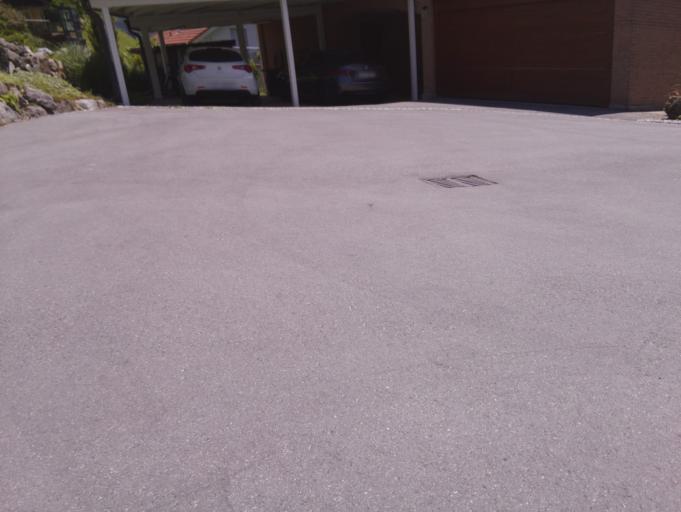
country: CH
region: Glarus
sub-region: Glarus
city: Glarus
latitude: 47.0403
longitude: 9.0565
